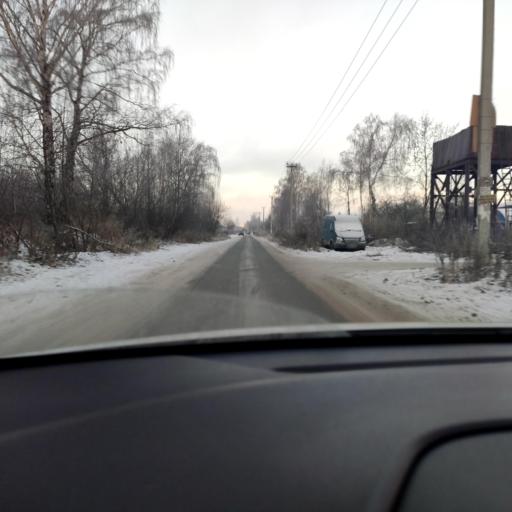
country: RU
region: Tatarstan
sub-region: Gorod Kazan'
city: Kazan
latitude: 55.8602
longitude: 49.0551
